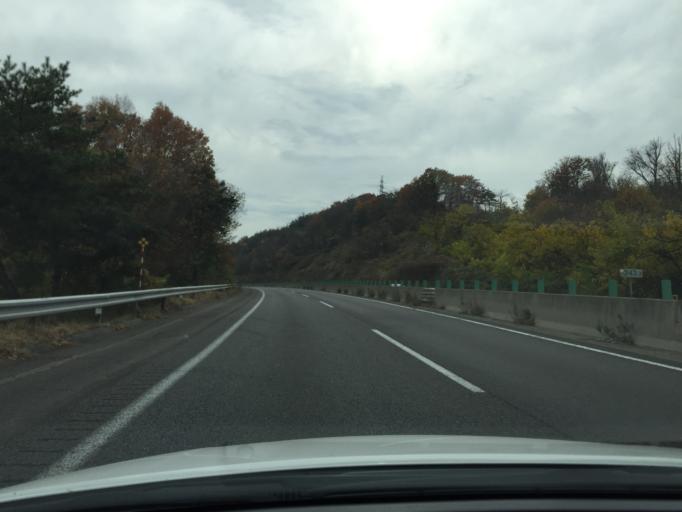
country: JP
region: Fukushima
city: Nihommatsu
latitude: 37.6541
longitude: 140.4330
